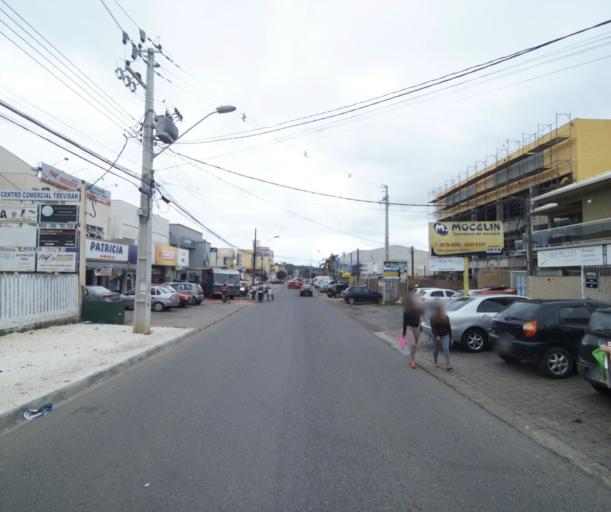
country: BR
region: Parana
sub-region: Quatro Barras
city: Quatro Barras
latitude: -25.3641
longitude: -49.1012
